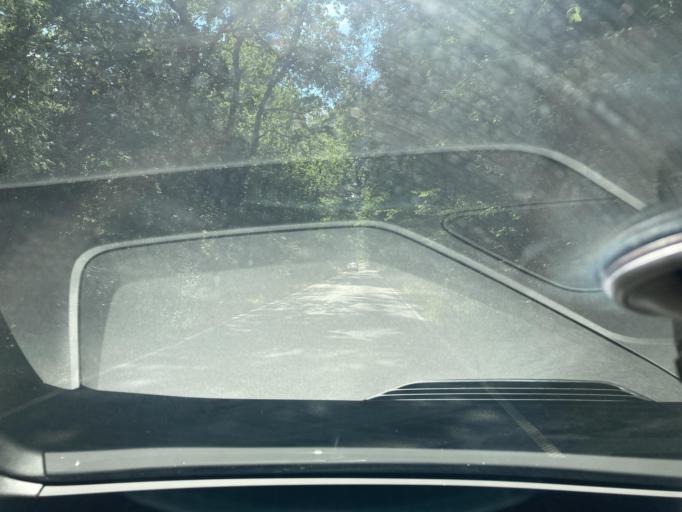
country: DE
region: Hesse
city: Obertshausen
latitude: 50.0996
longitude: 8.8718
